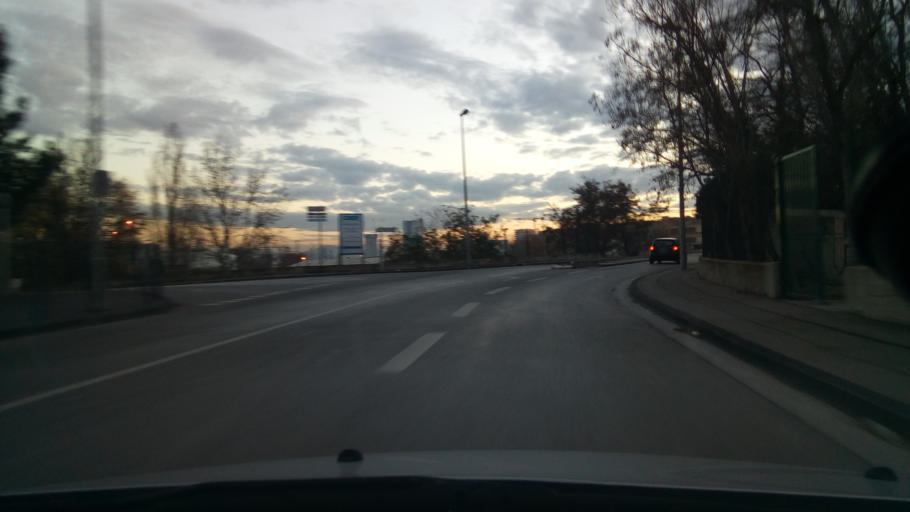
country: FR
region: Provence-Alpes-Cote d'Azur
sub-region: Departement des Bouches-du-Rhone
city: Marseille 14
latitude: 43.3328
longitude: 5.3678
